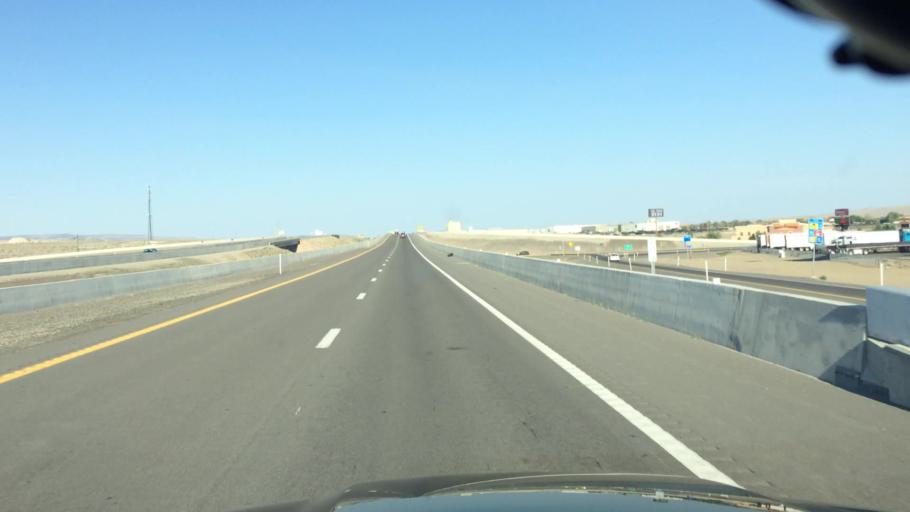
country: US
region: Nevada
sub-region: Lyon County
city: Fernley
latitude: 39.6163
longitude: -119.2683
